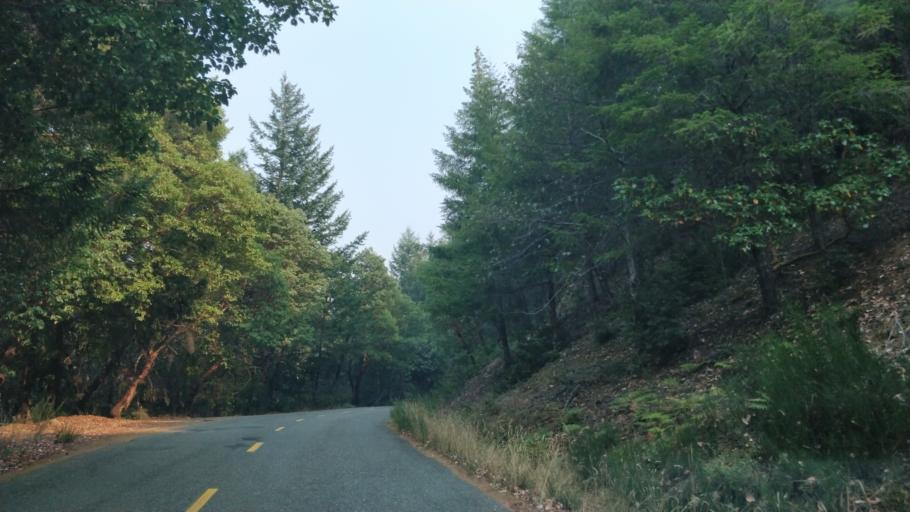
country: US
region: California
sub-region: Humboldt County
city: Rio Dell
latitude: 40.2625
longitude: -124.1054
